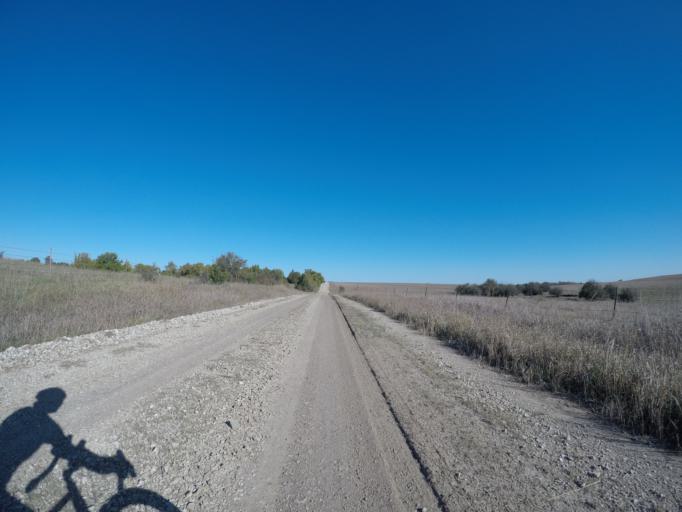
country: US
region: Kansas
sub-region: Wabaunsee County
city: Alma
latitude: 38.8731
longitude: -96.4097
